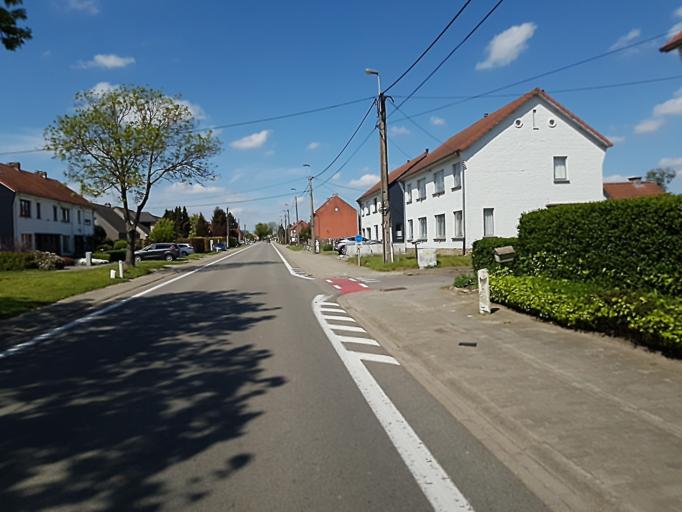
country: BE
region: Flanders
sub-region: Provincie Vlaams-Brabant
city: Tienen
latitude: 50.8234
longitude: 4.9244
